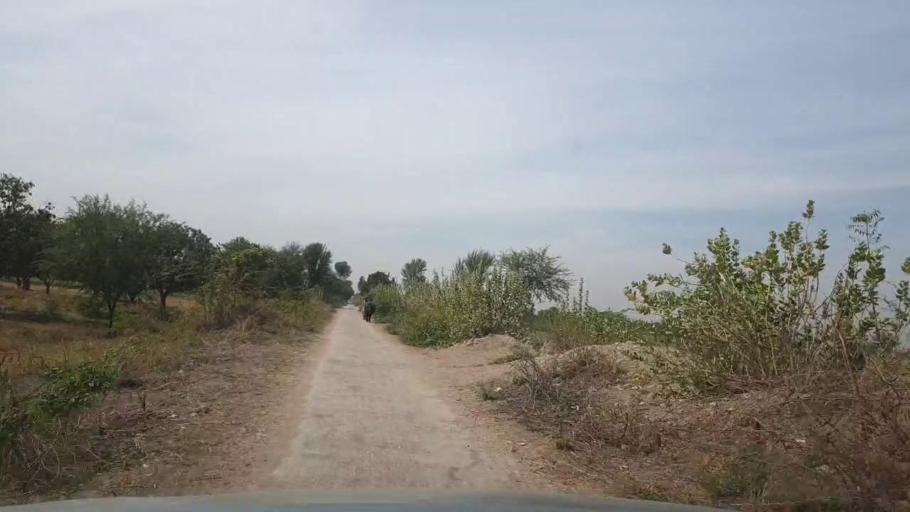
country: PK
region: Sindh
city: Nabisar
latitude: 25.0731
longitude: 69.5919
